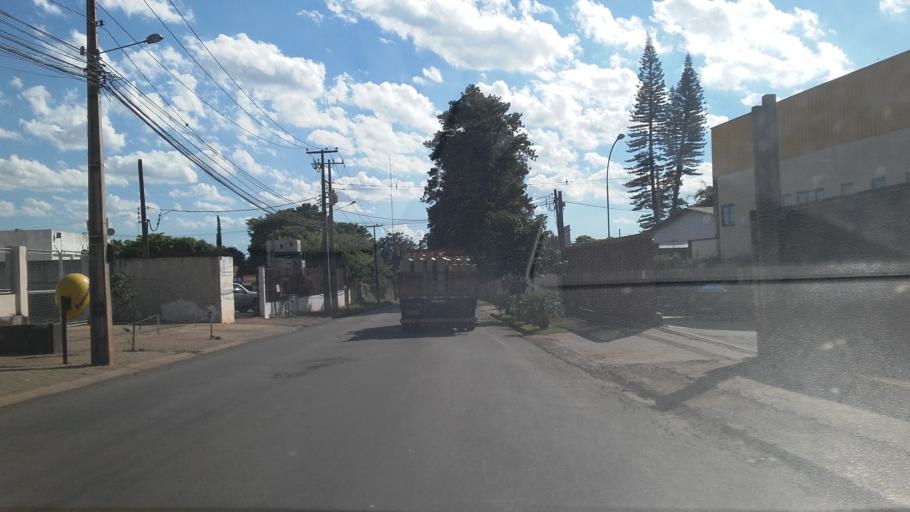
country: BR
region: Parana
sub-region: Londrina
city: Londrina
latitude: -23.2917
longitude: -51.2071
